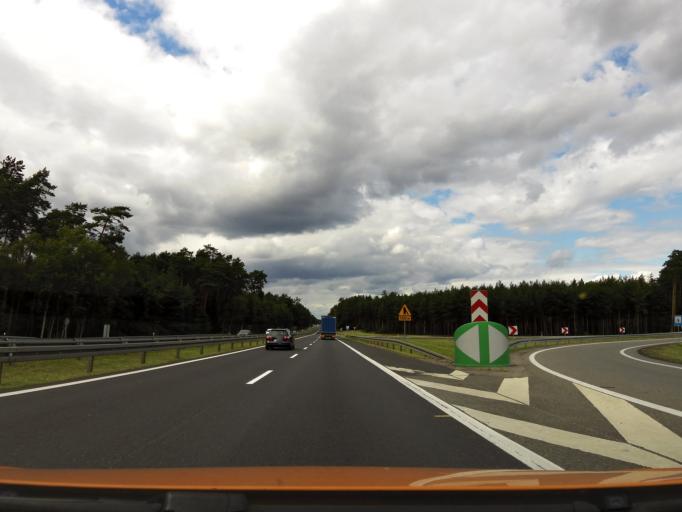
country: PL
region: West Pomeranian Voivodeship
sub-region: Powiat goleniowski
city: Goleniow
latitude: 53.5341
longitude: 14.8102
